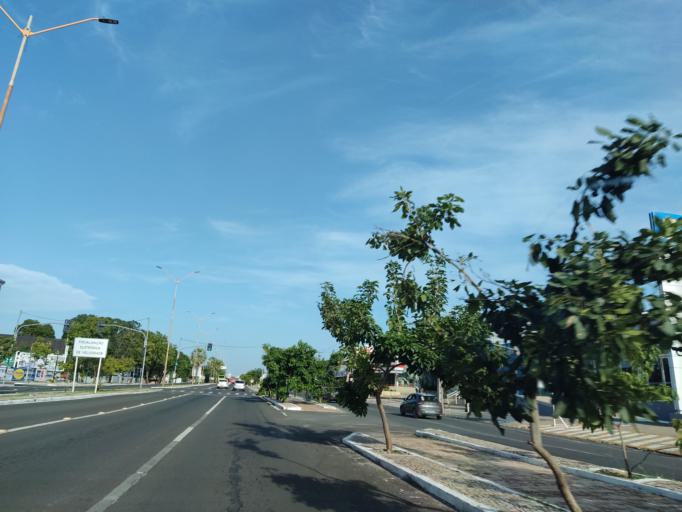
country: BR
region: Piaui
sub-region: Teresina
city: Teresina
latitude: -5.0806
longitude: -42.7842
